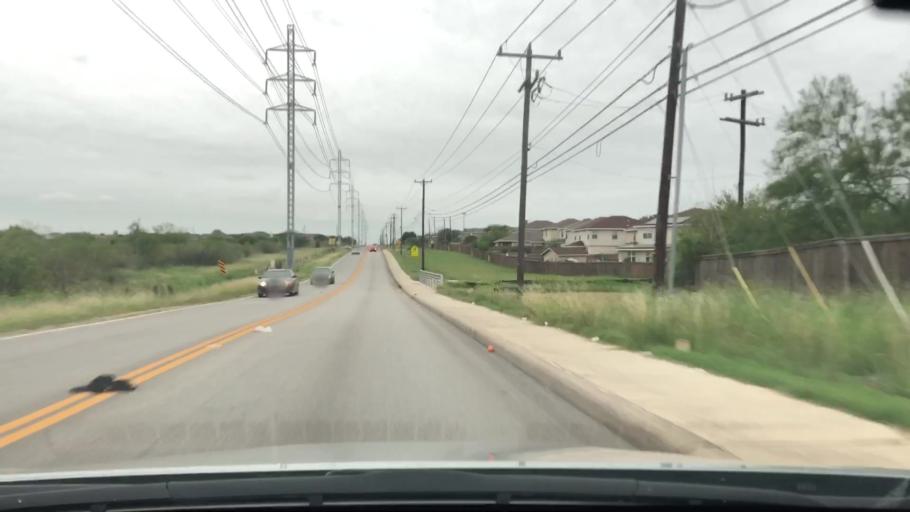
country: US
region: Texas
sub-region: Bexar County
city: Kirby
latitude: 29.4660
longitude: -98.3492
